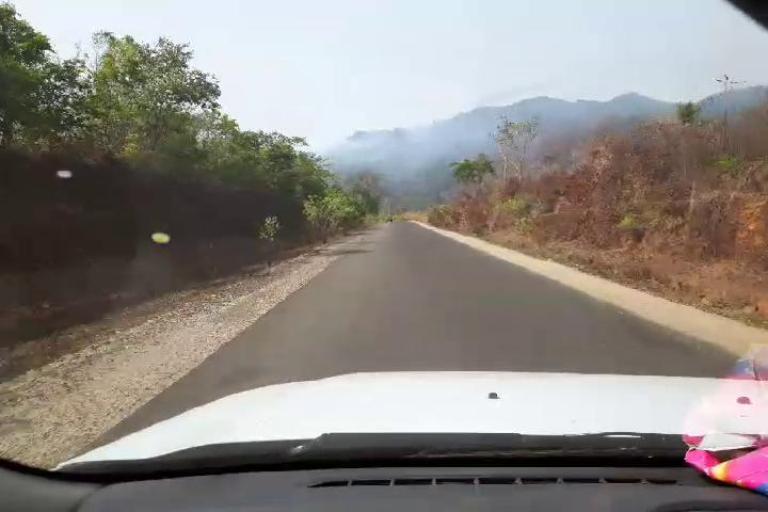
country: SL
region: Western Area
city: Waterloo
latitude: 8.2505
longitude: -13.1537
